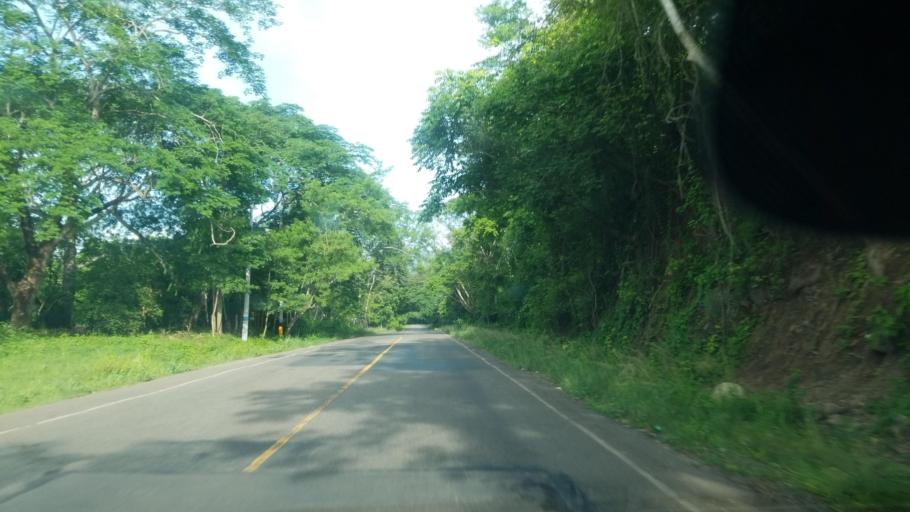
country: HN
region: Santa Barbara
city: Trinidad
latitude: 15.1372
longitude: -88.2261
